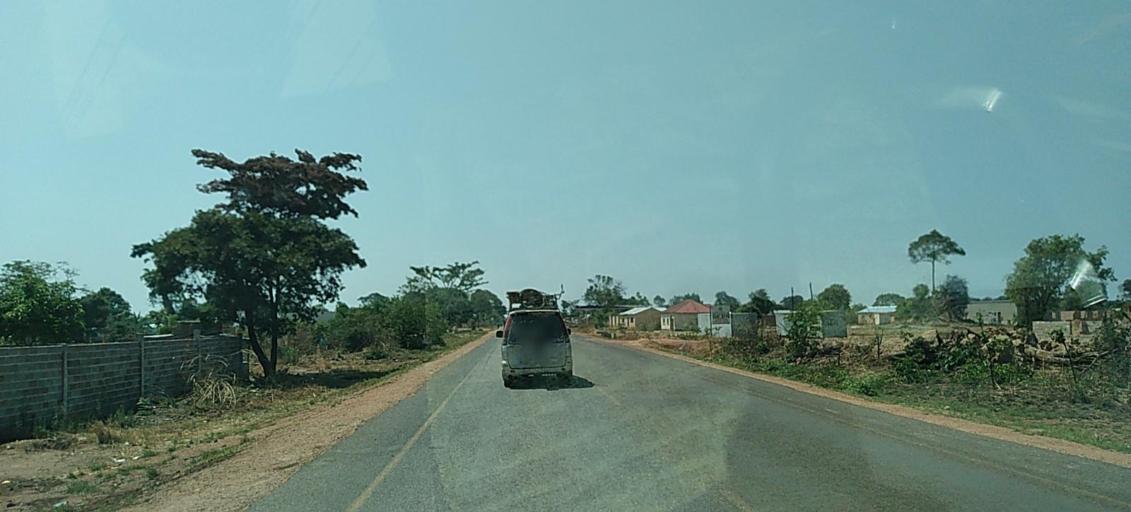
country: ZM
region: North-Western
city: Solwezi
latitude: -12.3051
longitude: 25.8368
